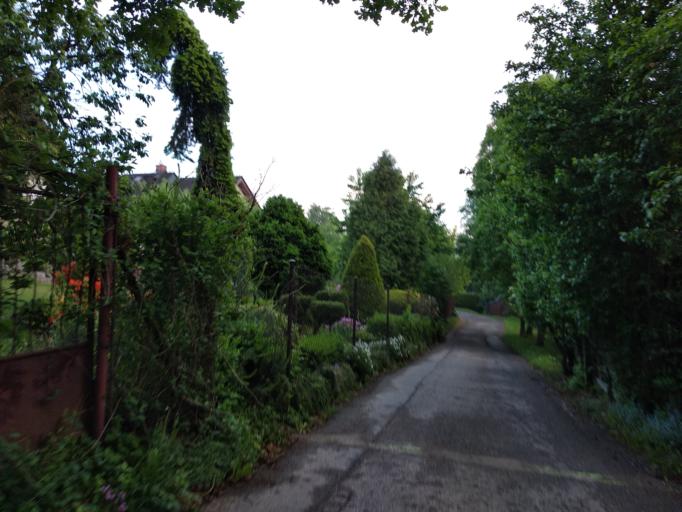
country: CZ
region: Moravskoslezsky
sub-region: Okres Frydek-Mistek
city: Frydek-Mistek
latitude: 49.6930
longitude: 18.3721
